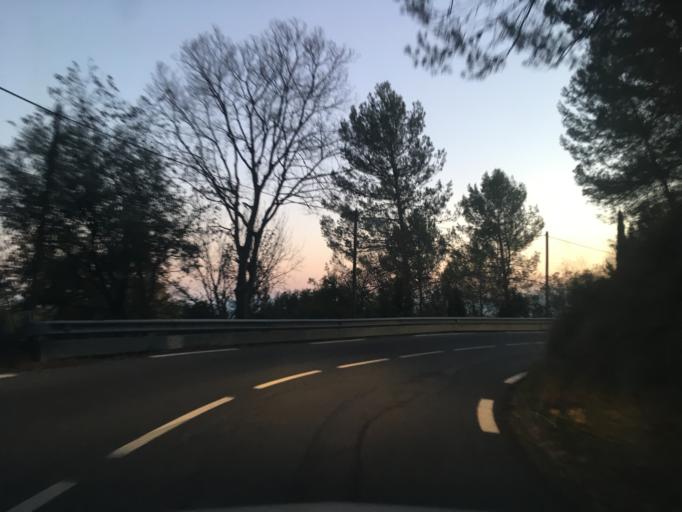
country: FR
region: Provence-Alpes-Cote d'Azur
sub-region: Departement du Var
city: Trans-en-Provence
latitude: 43.5349
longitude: 6.5033
